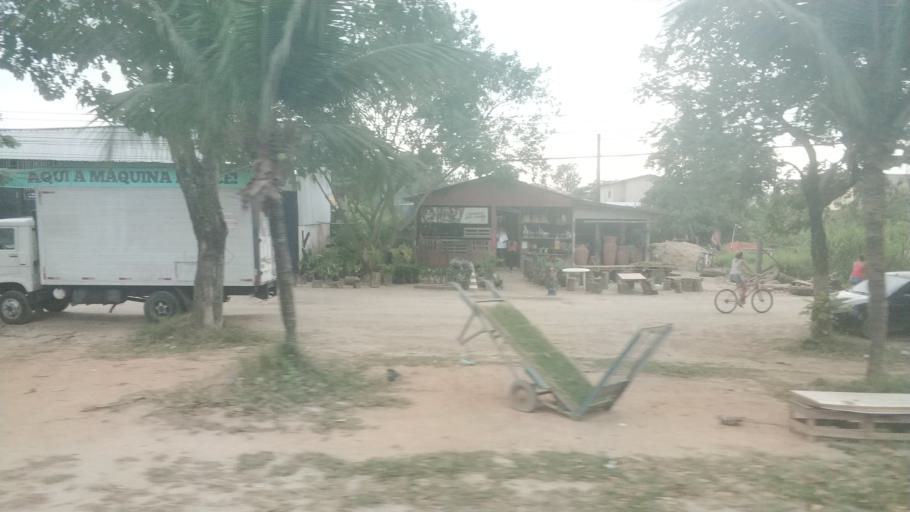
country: BR
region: Rio de Janeiro
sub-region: Seropedica
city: Seropedica
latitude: -22.8020
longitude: -43.6425
